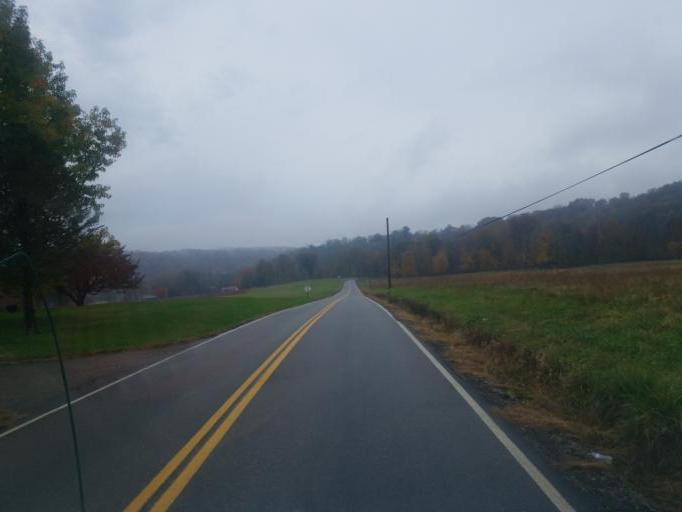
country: US
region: Ohio
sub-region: Morgan County
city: McConnelsville
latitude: 39.5582
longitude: -81.7855
